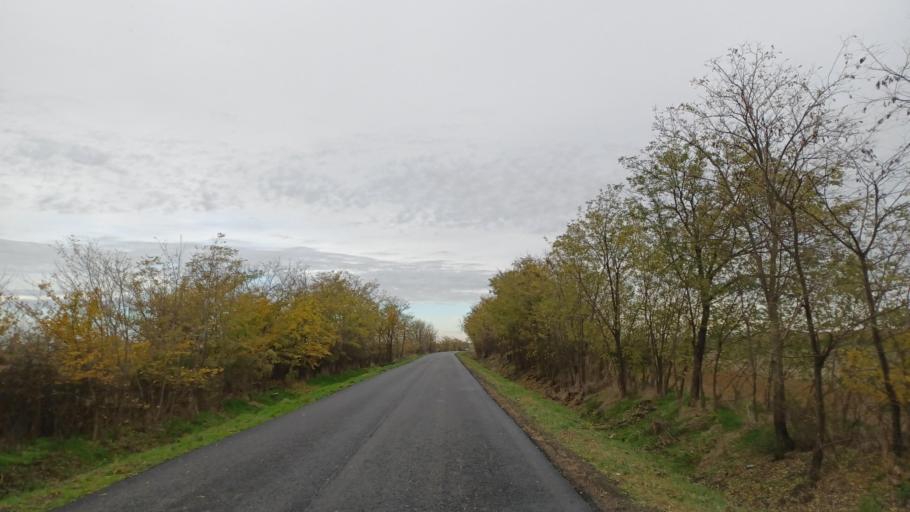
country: HU
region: Tolna
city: Tengelic
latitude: 46.5445
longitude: 18.7538
